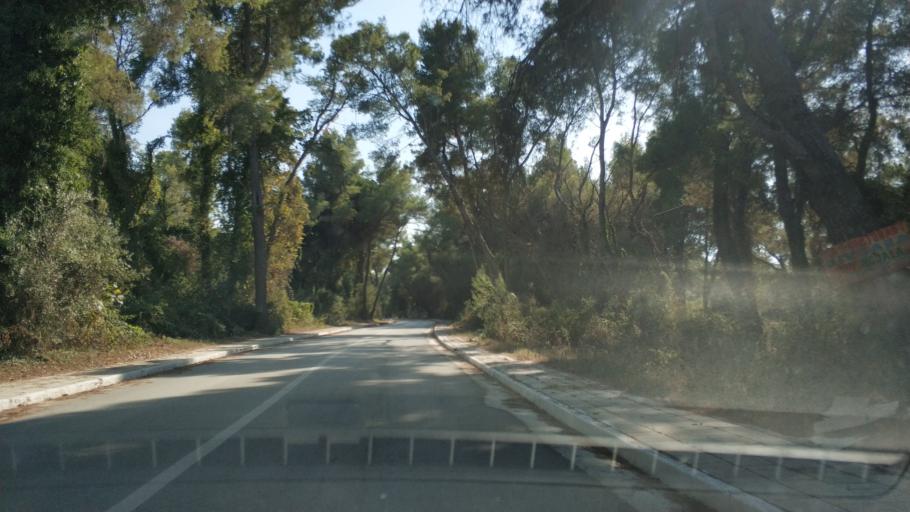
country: AL
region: Fier
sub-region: Rrethi i Lushnjes
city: Divjake
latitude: 40.9652
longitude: 19.4779
